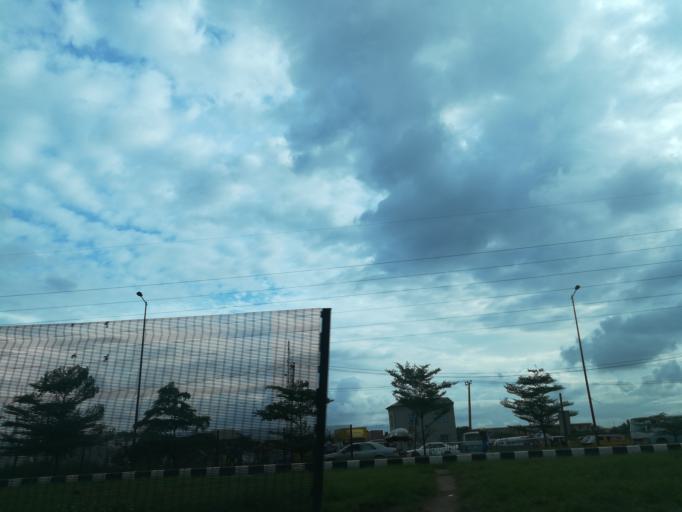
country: NG
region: Lagos
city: Ojota
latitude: 6.6108
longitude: 3.4205
